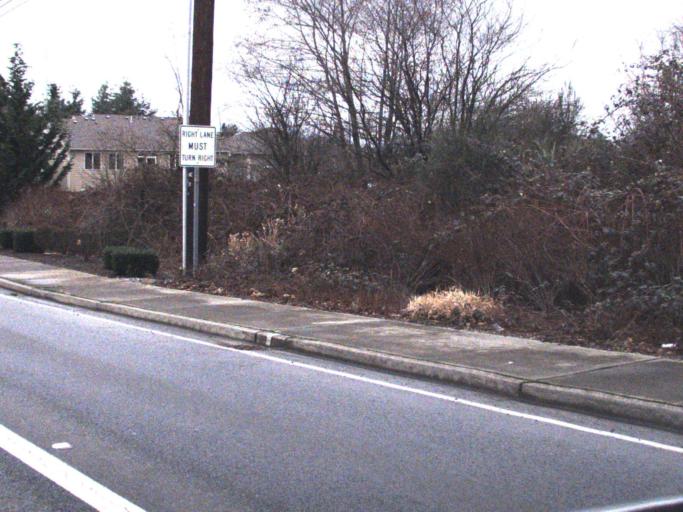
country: US
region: Washington
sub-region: Snohomish County
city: Sisco Heights
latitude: 48.1517
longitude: -122.1156
